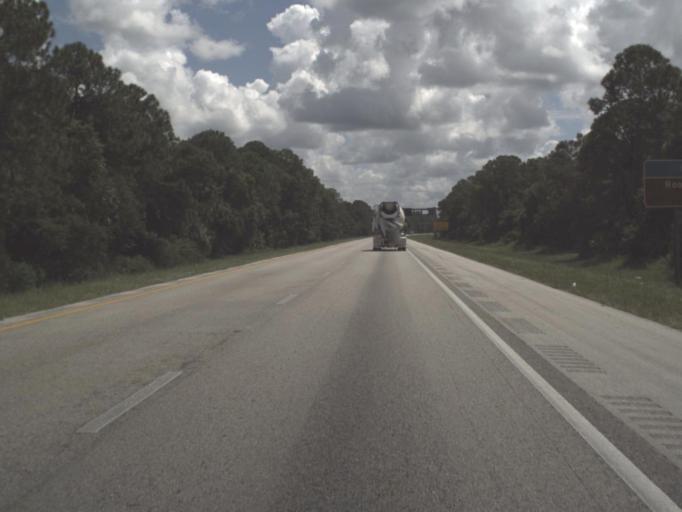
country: US
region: Florida
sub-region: Collier County
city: Golden Gate
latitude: 26.1636
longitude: -81.7088
